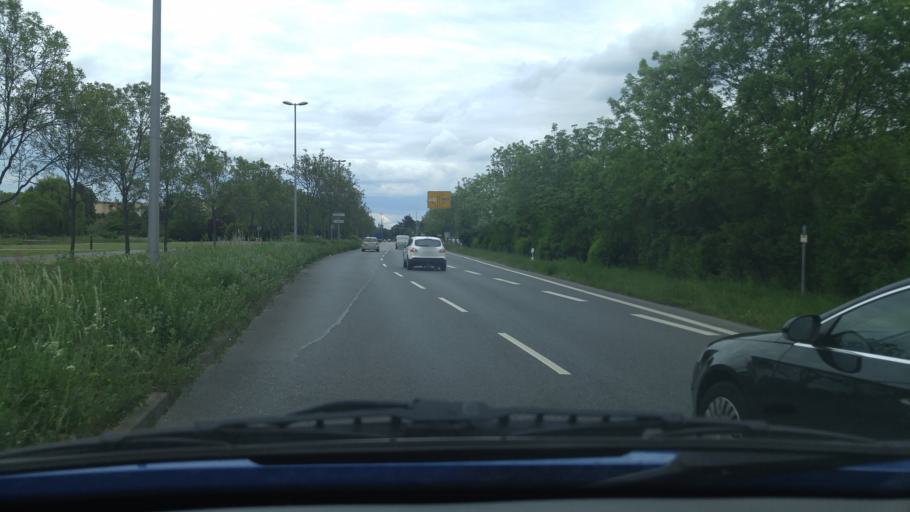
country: DE
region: Hesse
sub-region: Regierungsbezirk Darmstadt
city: Russelsheim
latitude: 49.9859
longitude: 8.4092
